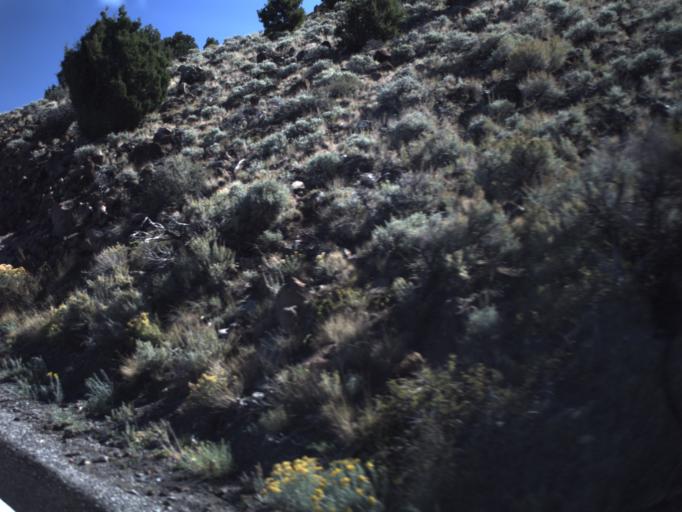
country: US
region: Utah
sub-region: Wayne County
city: Loa
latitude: 38.4784
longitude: -111.8288
